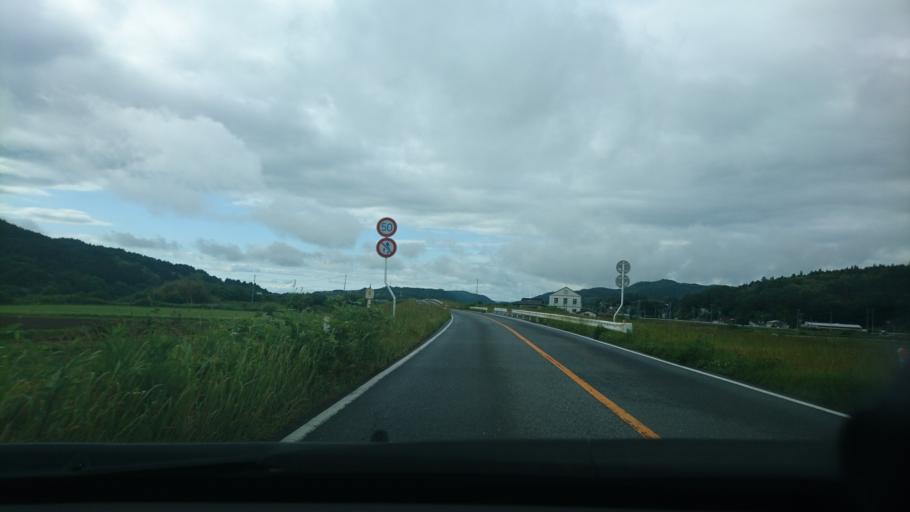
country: JP
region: Miyagi
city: Wakuya
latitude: 38.6379
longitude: 141.2887
